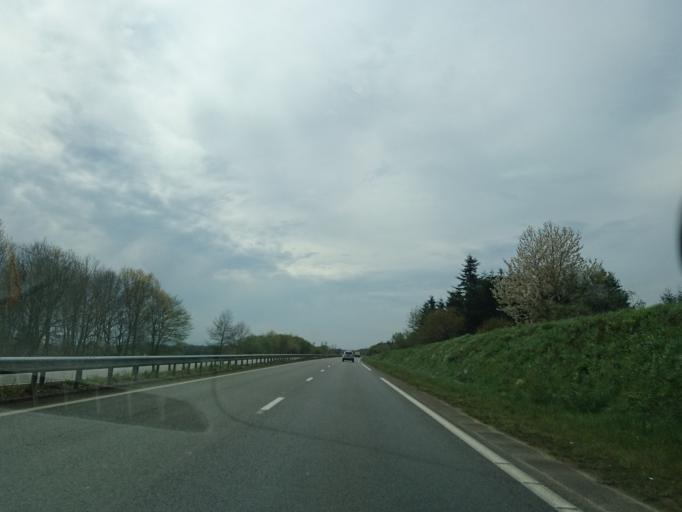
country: FR
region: Brittany
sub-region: Departement des Cotes-d'Armor
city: Plelan-le-Petit
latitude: 48.4210
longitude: -2.2646
